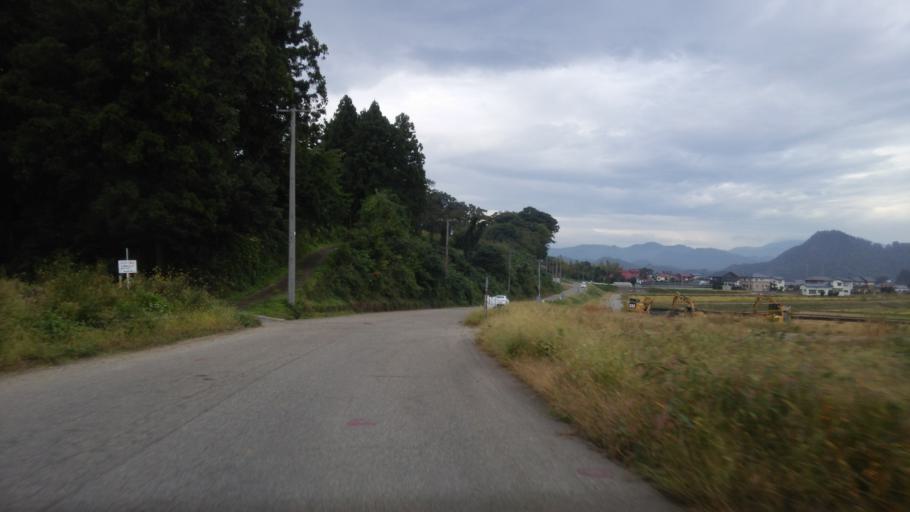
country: JP
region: Fukushima
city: Kitakata
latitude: 37.4548
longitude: 139.9289
